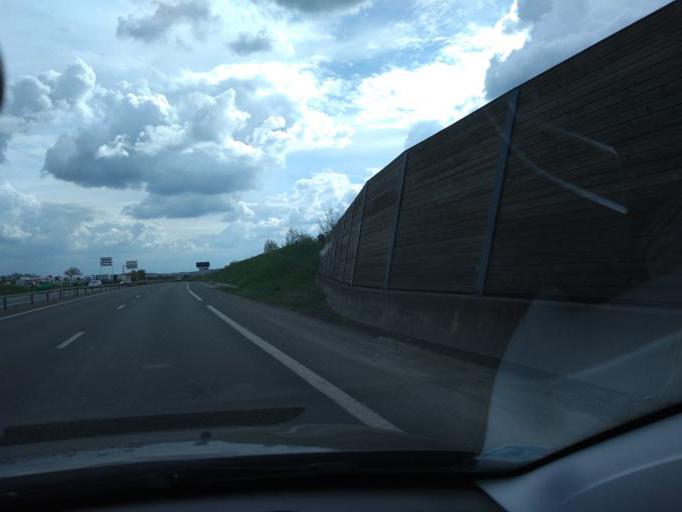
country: FR
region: Pays de la Loire
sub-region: Departement de Maine-et-Loire
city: Beaucouze
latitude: 47.5065
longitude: -0.6186
